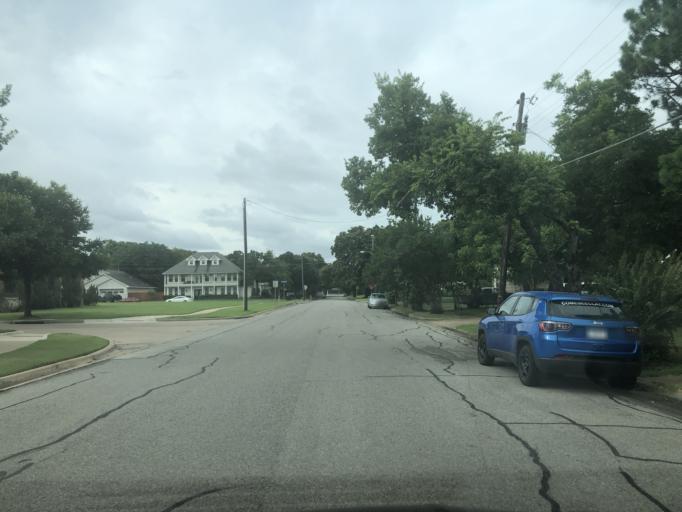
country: US
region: Texas
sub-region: Dallas County
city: Irving
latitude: 32.8115
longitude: -96.9449
